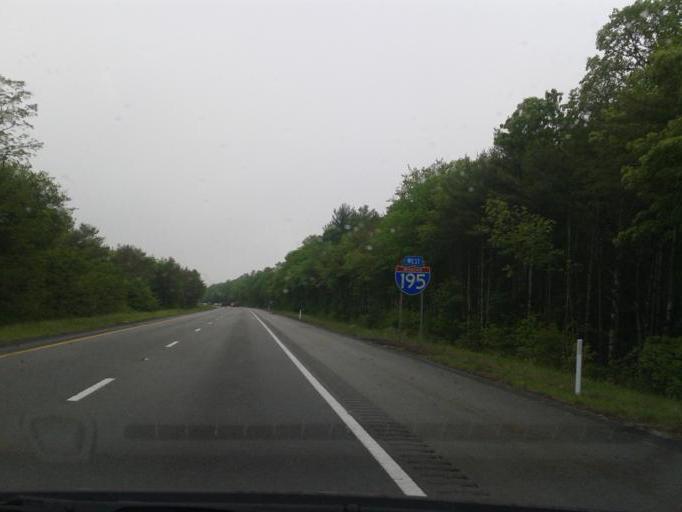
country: US
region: Massachusetts
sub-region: Plymouth County
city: Mattapoisett
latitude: 41.6655
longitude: -70.8457
